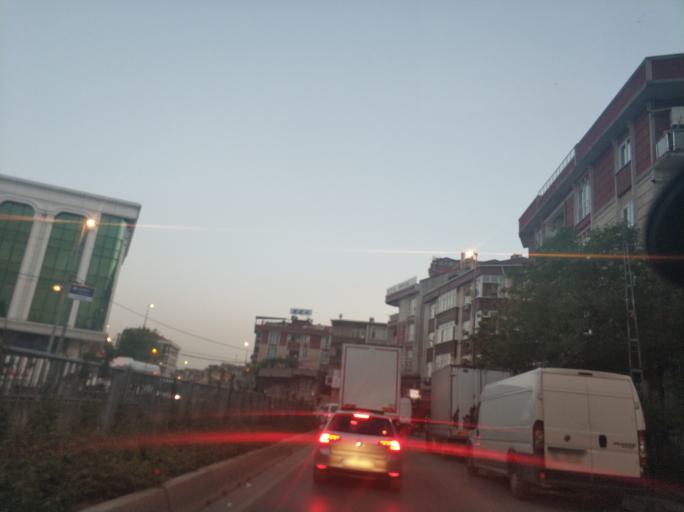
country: TR
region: Istanbul
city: Bagcilar
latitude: 41.0523
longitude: 28.8478
